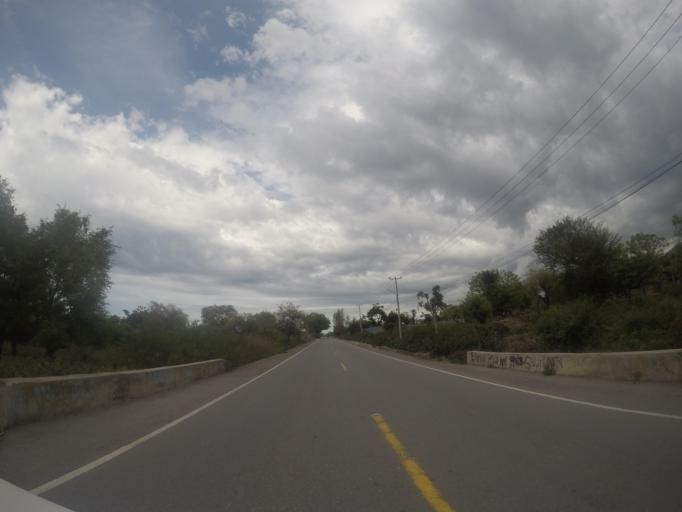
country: TL
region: Liquica
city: Liquica
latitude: -8.5985
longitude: 125.3077
